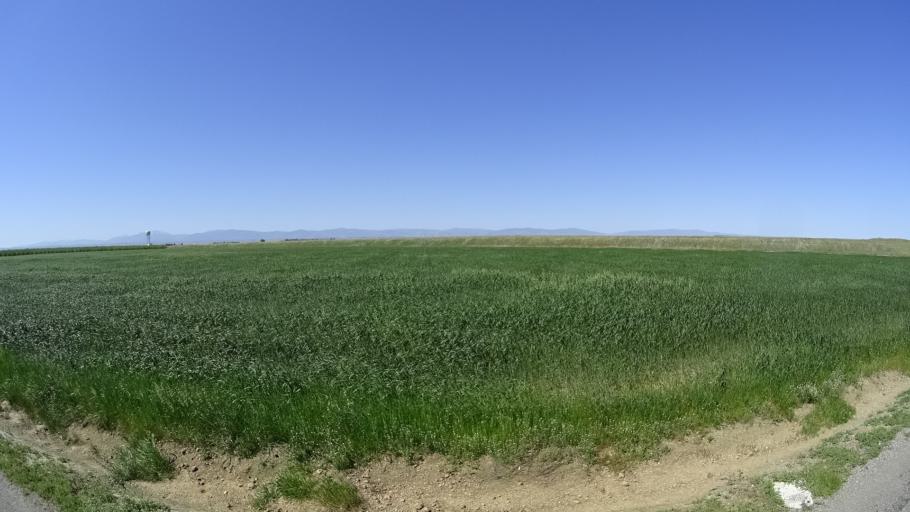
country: US
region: California
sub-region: Glenn County
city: Orland
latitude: 39.6887
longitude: -122.2341
